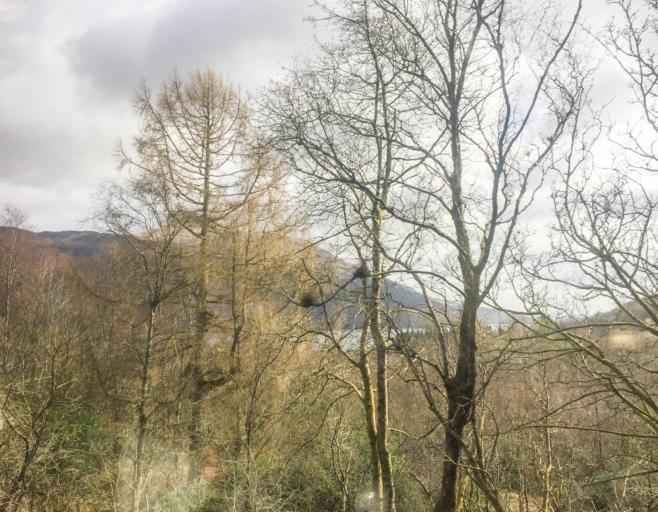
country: GB
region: Scotland
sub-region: Argyll and Bute
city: Garelochhead
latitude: 56.2055
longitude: -4.7152
